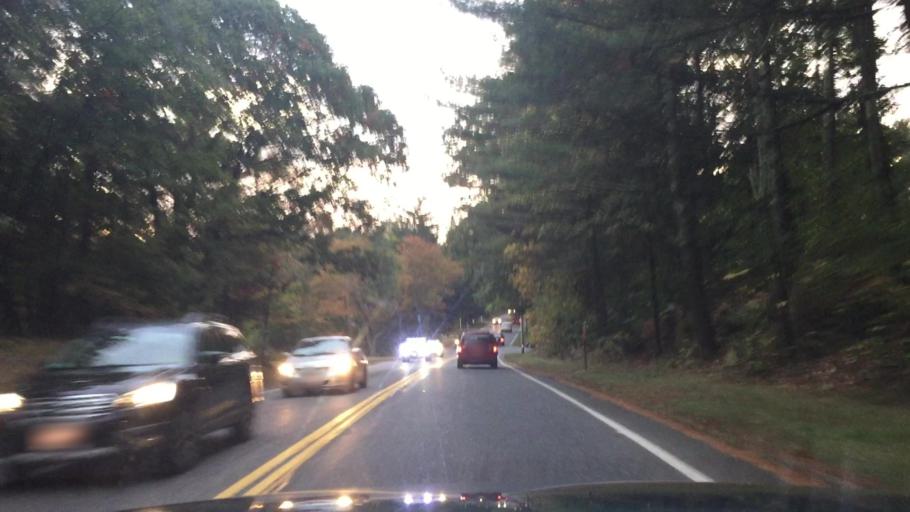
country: US
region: Massachusetts
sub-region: Norfolk County
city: Medfield
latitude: 42.1651
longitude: -71.2868
